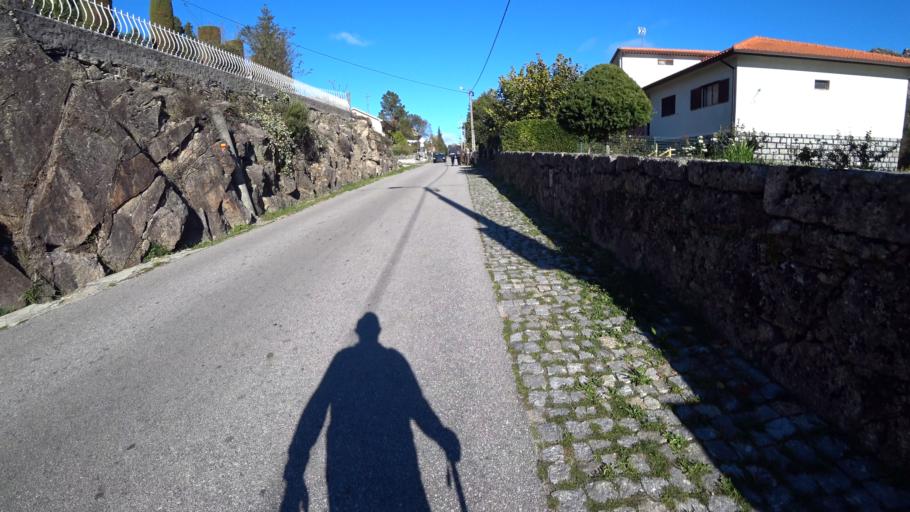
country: PT
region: Braga
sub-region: Terras de Bouro
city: Antas
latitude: 41.7582
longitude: -8.1940
